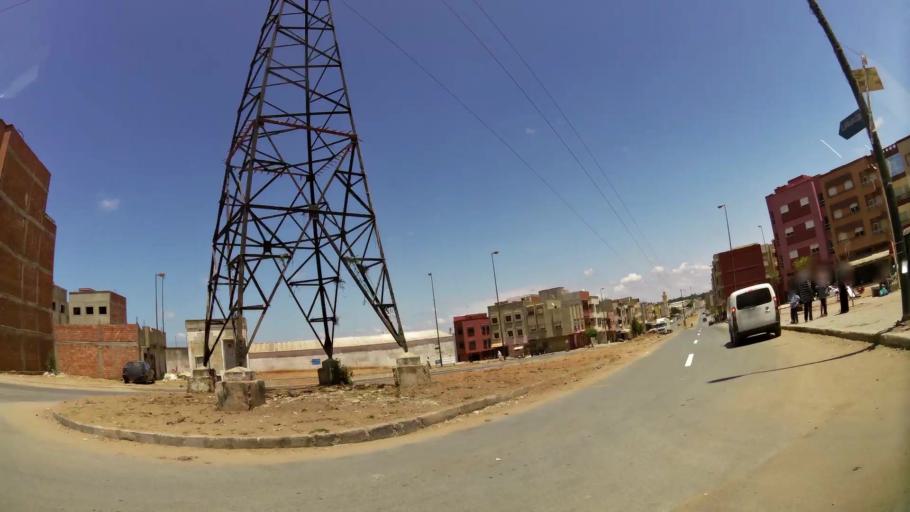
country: MA
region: Gharb-Chrarda-Beni Hssen
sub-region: Kenitra Province
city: Kenitra
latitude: 34.2341
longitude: -6.6167
